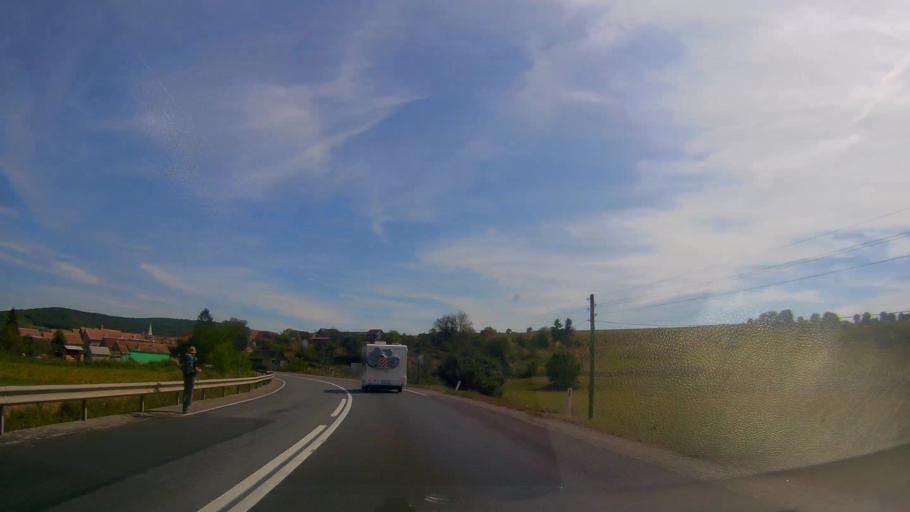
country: RO
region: Mures
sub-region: Comuna Balauseri
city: Chendu
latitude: 46.3959
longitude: 24.7127
